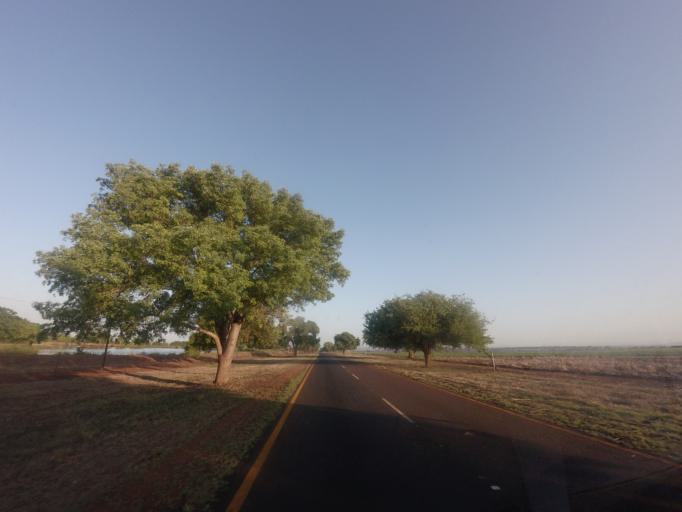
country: ZA
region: Mpumalanga
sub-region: Ehlanzeni District
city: Komatipoort
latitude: -25.3769
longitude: 31.9070
